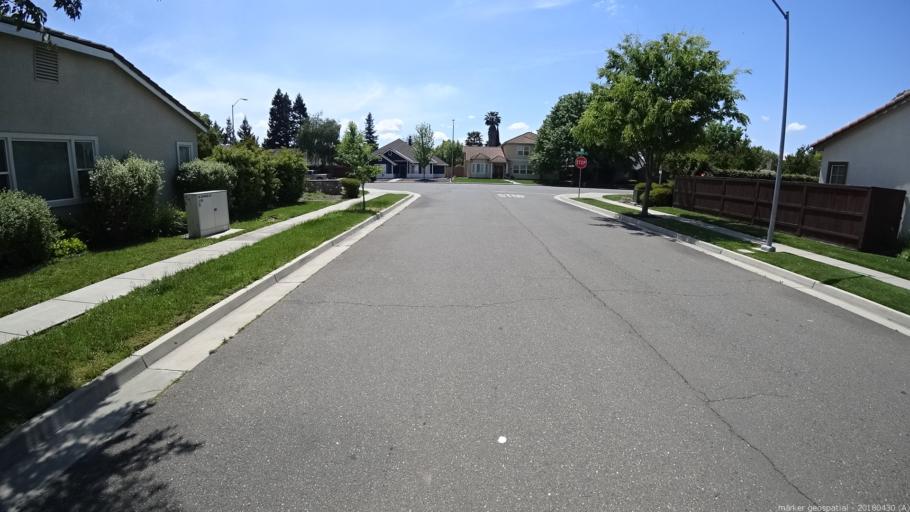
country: US
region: California
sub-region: Yolo County
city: West Sacramento
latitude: 38.5464
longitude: -121.5300
